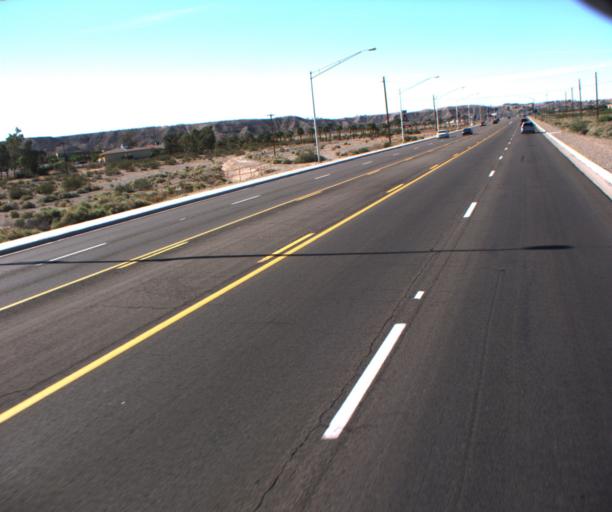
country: US
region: Arizona
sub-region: Mohave County
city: Bullhead City
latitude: 35.0652
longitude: -114.5893
